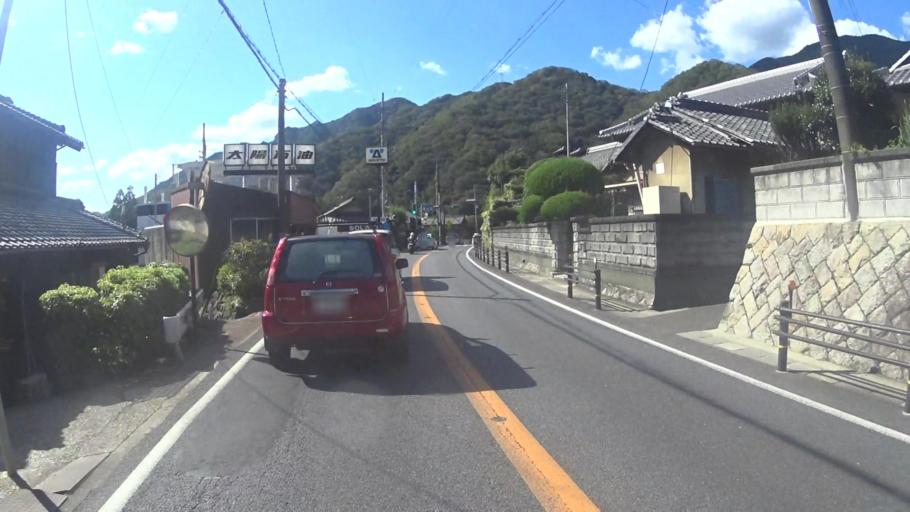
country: JP
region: Mie
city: Ueno-ebisumachi
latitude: 34.7710
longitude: 135.9958
